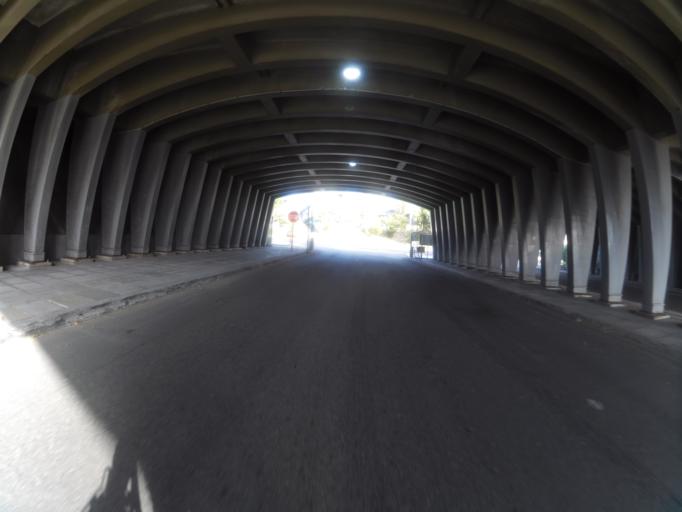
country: AU
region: Western Australia
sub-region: Fremantle
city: North Fremantle
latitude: -32.0448
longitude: 115.7514
